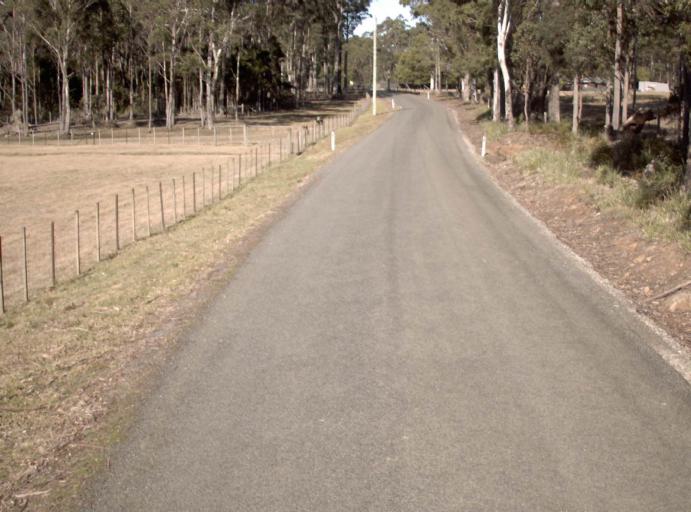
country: AU
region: Tasmania
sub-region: Launceston
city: Mayfield
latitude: -41.3137
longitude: 147.2013
